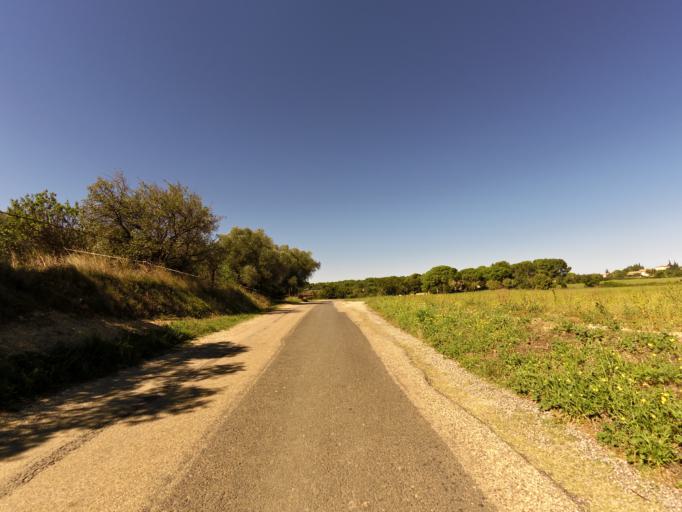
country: FR
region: Languedoc-Roussillon
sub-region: Departement du Gard
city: Mus
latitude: 43.7343
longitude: 4.2019
